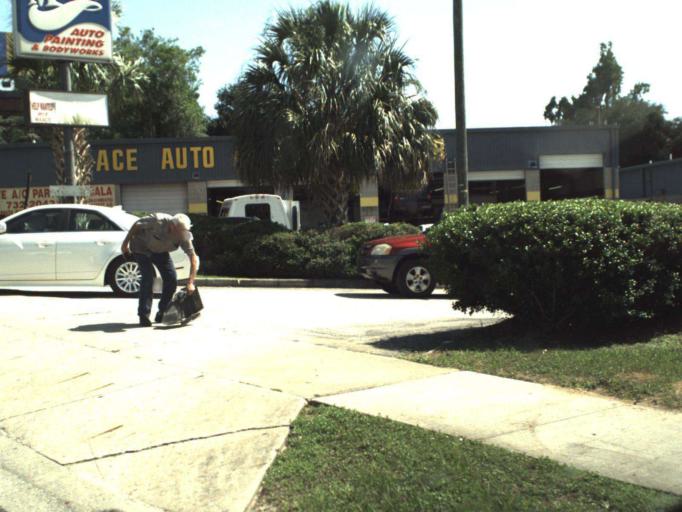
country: US
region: Florida
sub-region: Marion County
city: Ocala
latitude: 29.1672
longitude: -82.1375
